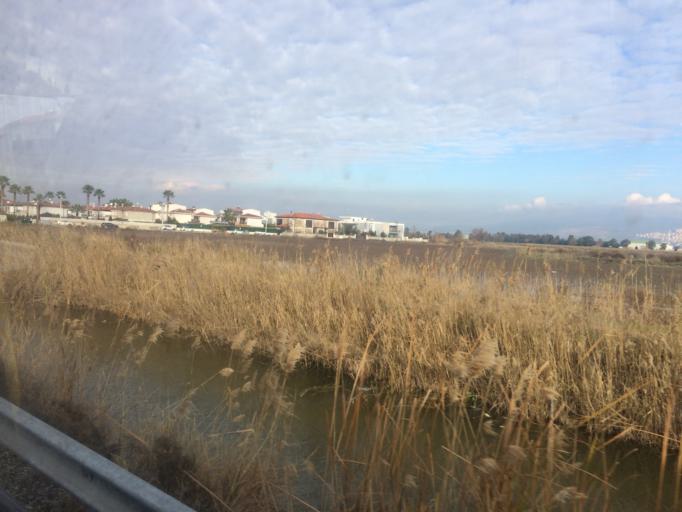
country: TR
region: Izmir
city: Menemen
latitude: 38.5001
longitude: 26.9600
